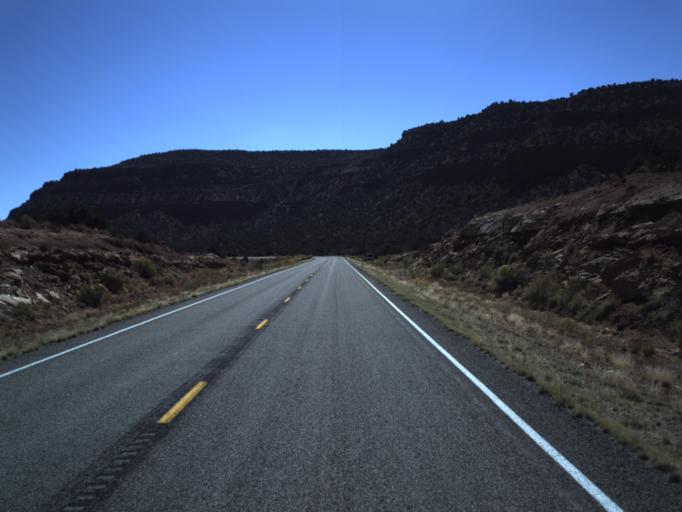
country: US
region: Utah
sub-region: San Juan County
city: Blanding
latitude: 37.6399
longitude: -110.1091
